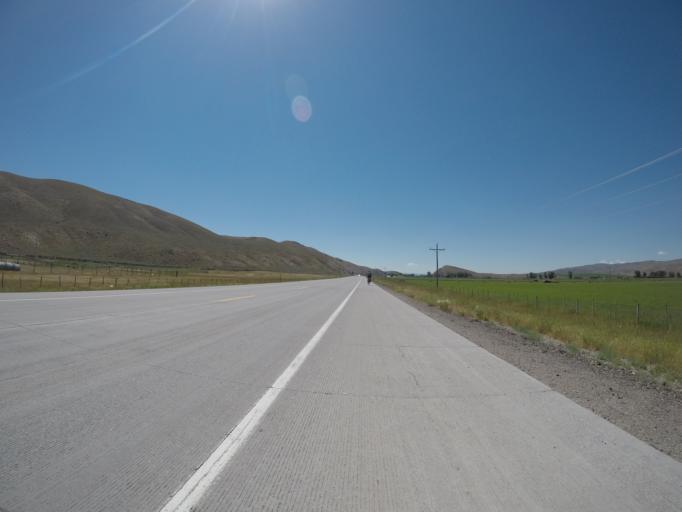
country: US
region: Idaho
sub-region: Bear Lake County
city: Montpelier
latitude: 42.1496
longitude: -110.9789
